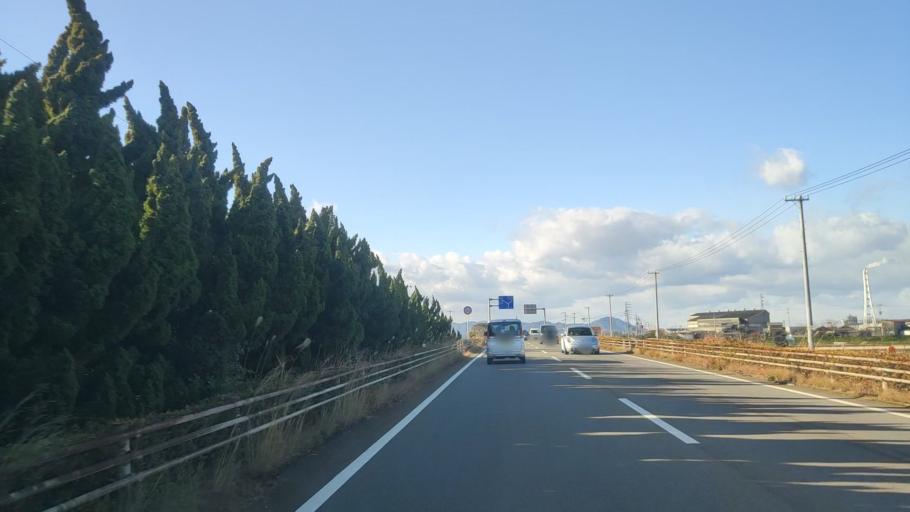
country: JP
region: Ehime
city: Saijo
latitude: 33.9174
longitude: 133.1276
